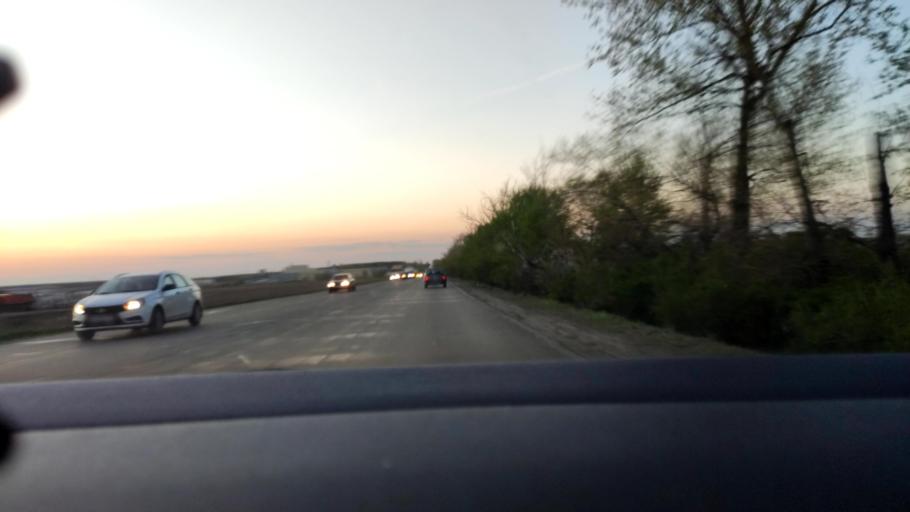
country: RU
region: Voronezj
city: Maslovka
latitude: 51.5422
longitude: 39.2864
